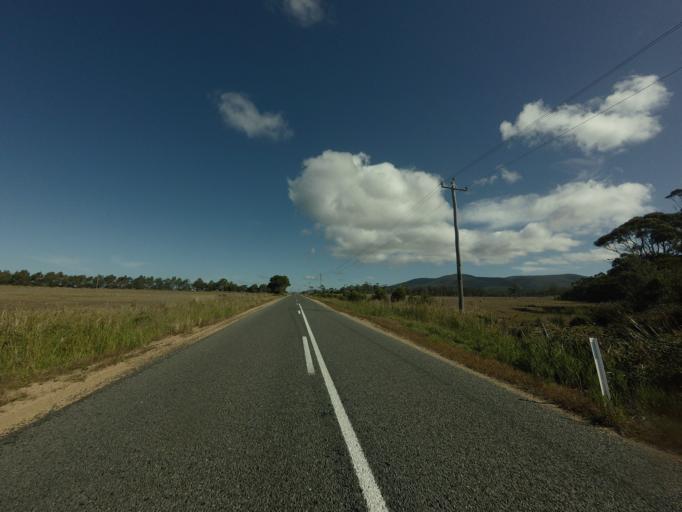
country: AU
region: Tasmania
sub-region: Break O'Day
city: St Helens
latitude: -41.7597
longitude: 148.2732
